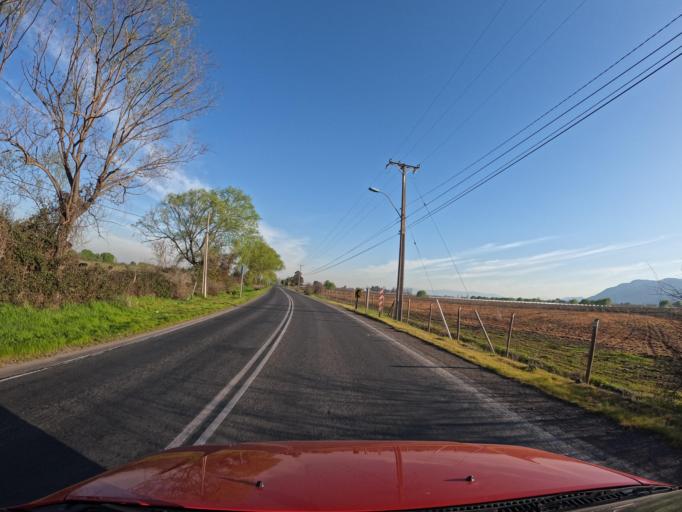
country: CL
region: Maule
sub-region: Provincia de Curico
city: Rauco
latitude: -34.8905
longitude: -71.2741
